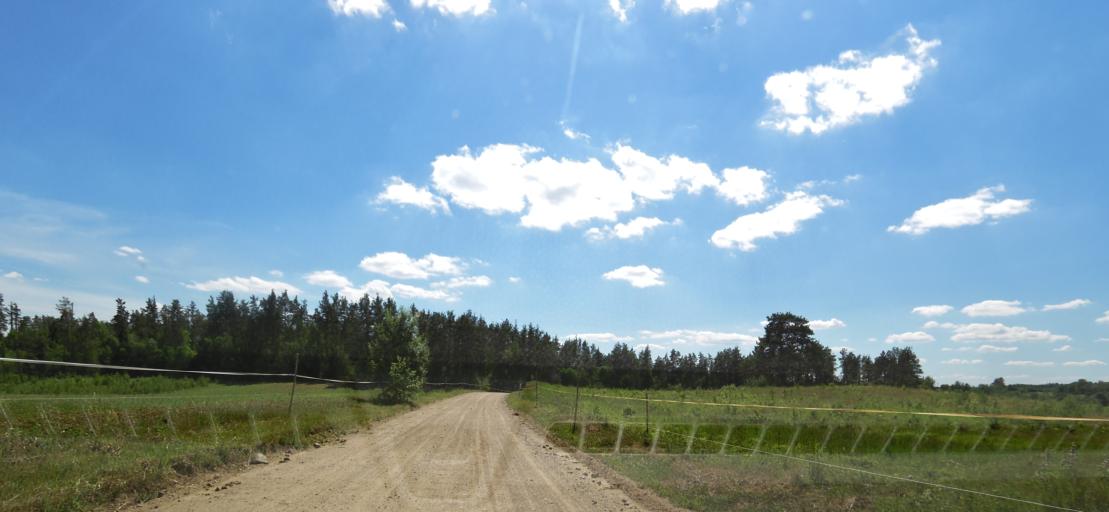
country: LT
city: Nemencine
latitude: 54.8610
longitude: 25.3485
